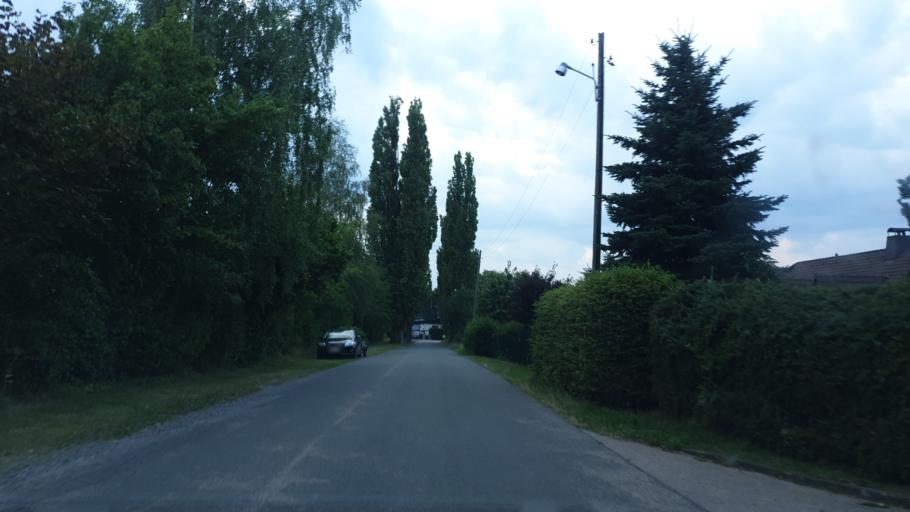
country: DE
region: Saxony
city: Lugau
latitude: 50.7364
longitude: 12.7301
